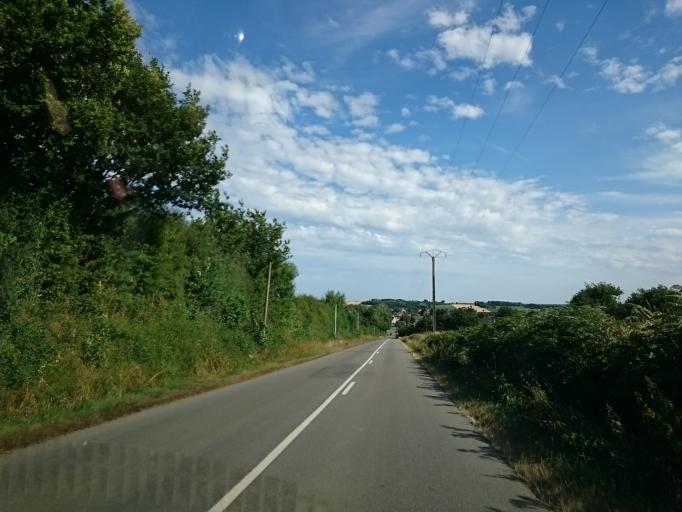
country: FR
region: Brittany
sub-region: Departement d'Ille-et-Vilaine
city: Pance
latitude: 47.9024
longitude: -1.6163
